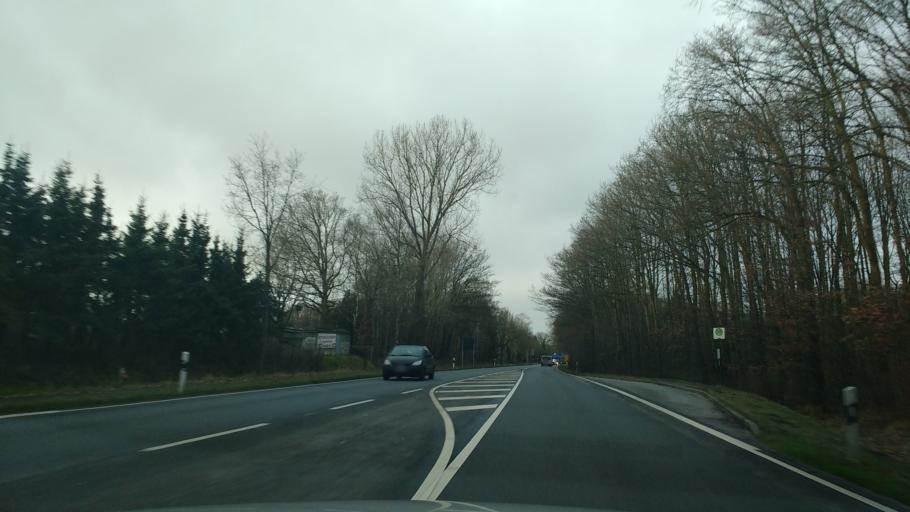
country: DE
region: Schleswig-Holstein
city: Itzehoe
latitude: 53.9015
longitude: 9.5103
